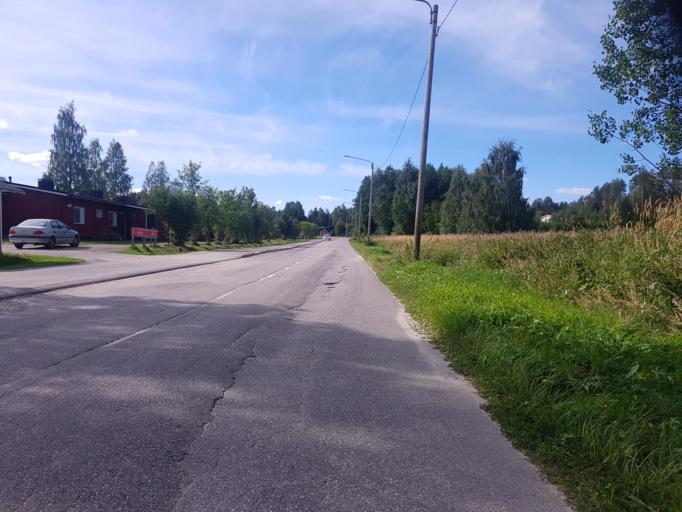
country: FI
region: Kainuu
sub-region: Kehys-Kainuu
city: Kuhmo
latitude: 64.1260
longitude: 29.5445
